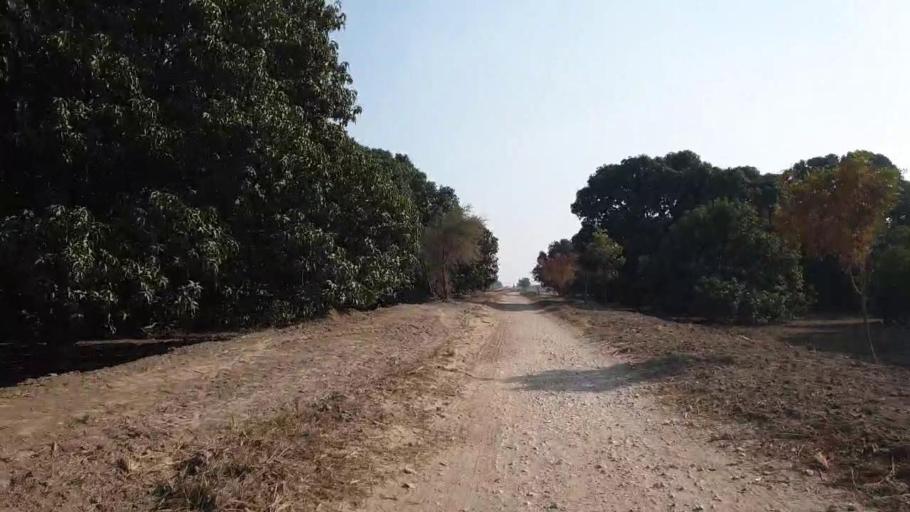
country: PK
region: Sindh
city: Tando Adam
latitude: 25.6015
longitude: 68.6161
